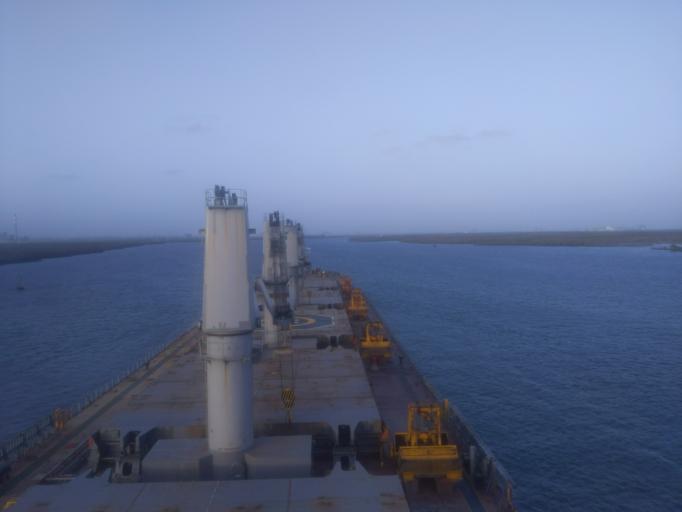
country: PK
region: Sindh
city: Malir Cantonment
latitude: 24.7824
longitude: 67.2428
